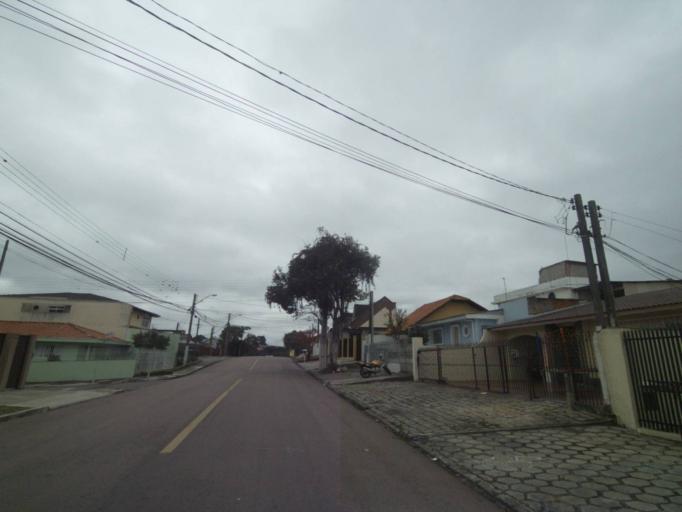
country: BR
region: Parana
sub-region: Curitiba
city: Curitiba
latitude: -25.4969
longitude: -49.2813
